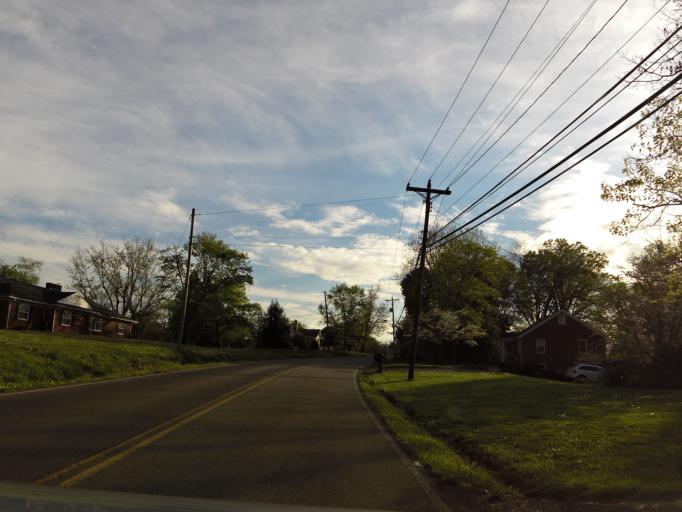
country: US
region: Tennessee
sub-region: Blount County
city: Maryville
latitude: 35.7179
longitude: -84.0056
